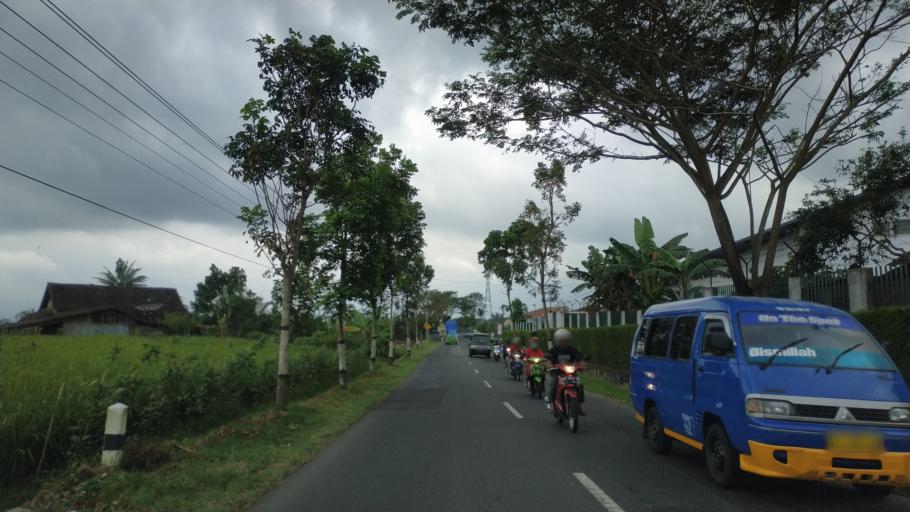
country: ID
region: Central Java
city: Magelang
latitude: -7.2866
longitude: 110.1228
